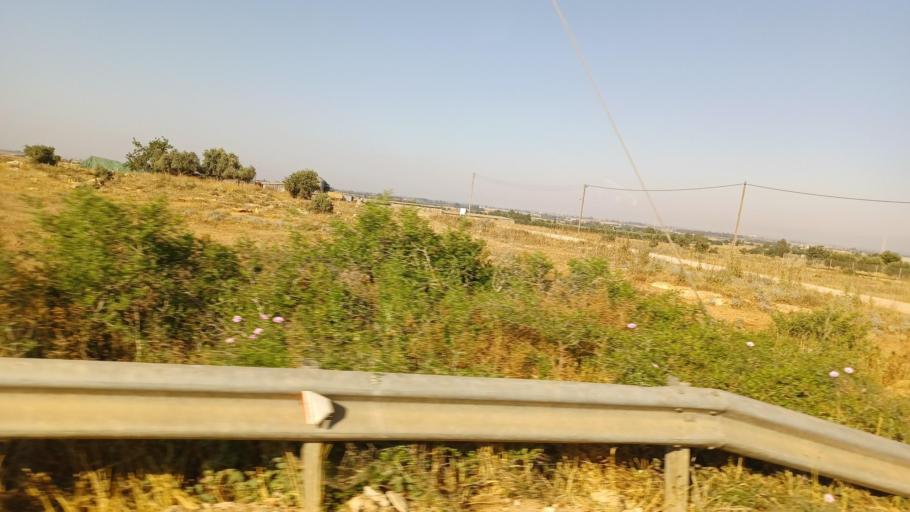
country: CY
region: Ammochostos
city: Frenaros
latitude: 35.0607
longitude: 33.9057
